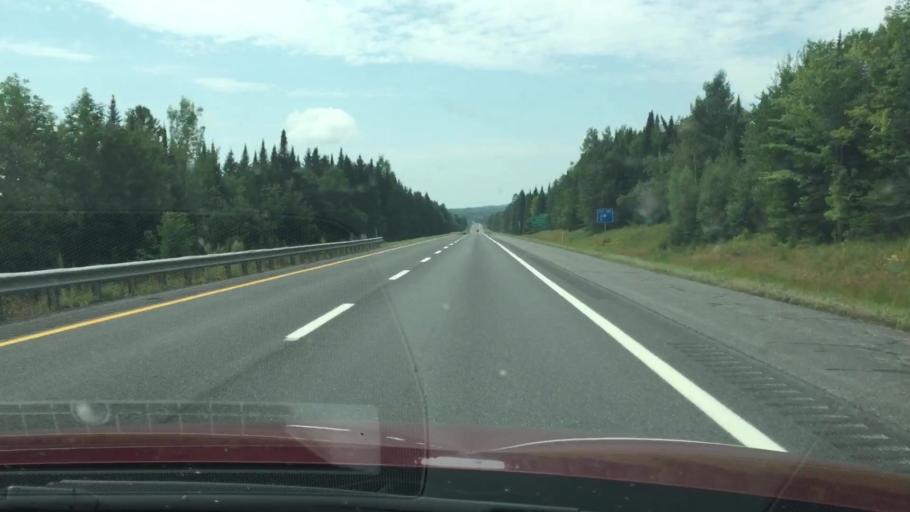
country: US
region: Maine
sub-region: Aroostook County
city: Hodgdon
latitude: 46.1168
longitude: -68.1331
